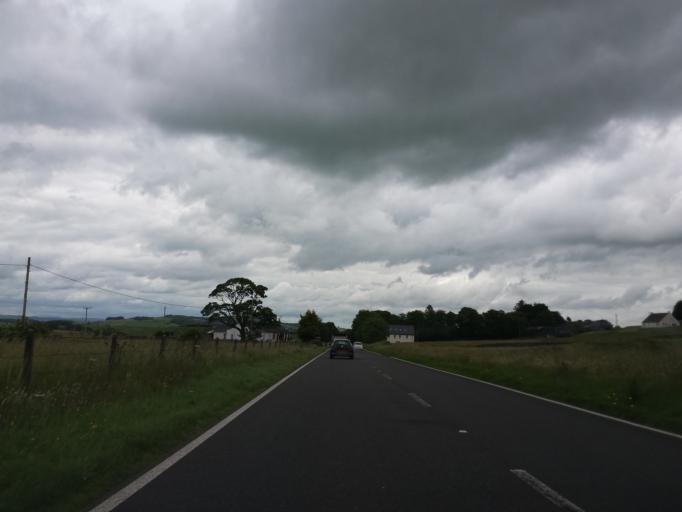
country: GB
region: Scotland
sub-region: Dumfries and Galloway
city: Dalbeattie
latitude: 55.0471
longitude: -3.7881
